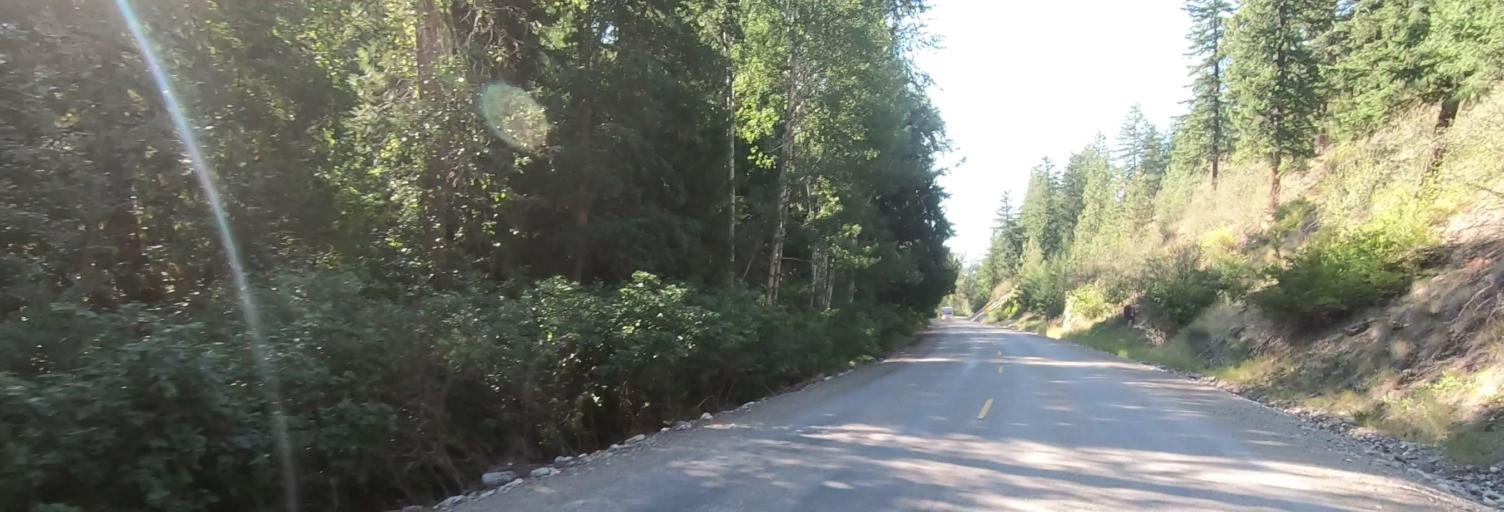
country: US
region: Washington
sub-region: Chelan County
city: Granite Falls
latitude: 48.5533
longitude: -120.3356
